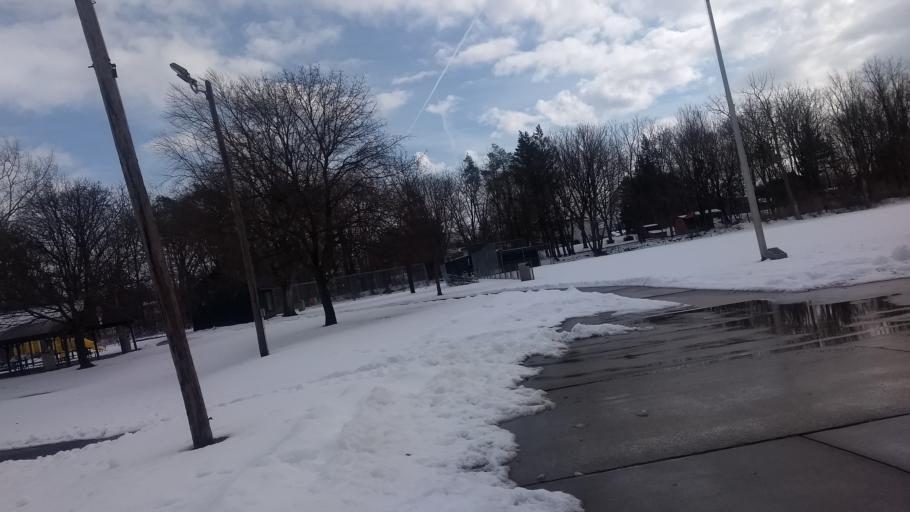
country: US
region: New York
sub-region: Livingston County
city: Geneseo
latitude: 42.7969
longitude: -77.8051
